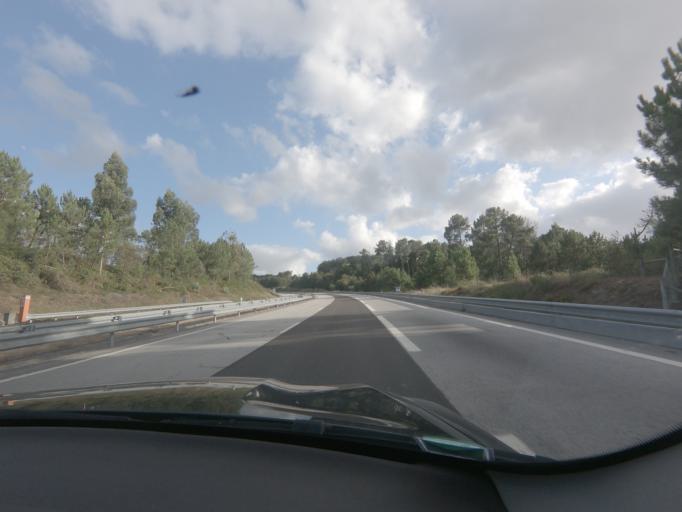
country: PT
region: Viseu
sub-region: Viseu
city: Campo
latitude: 40.7400
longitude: -7.9244
